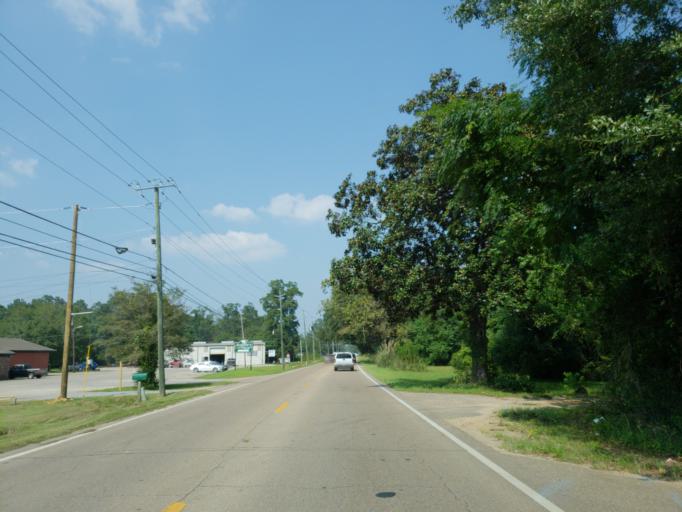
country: US
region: Mississippi
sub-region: Jones County
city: Ellisville
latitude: 31.6523
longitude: -89.1709
